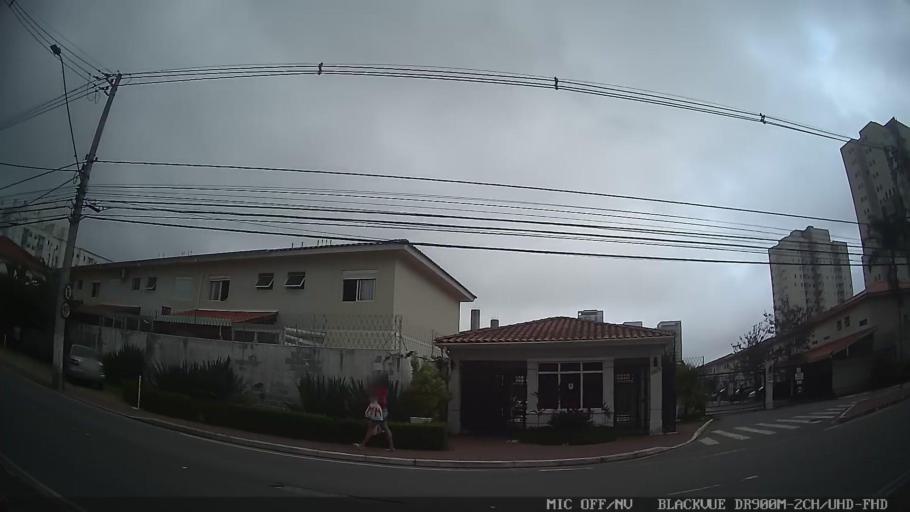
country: BR
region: Sao Paulo
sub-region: Mogi das Cruzes
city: Mogi das Cruzes
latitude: -23.5120
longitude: -46.1795
